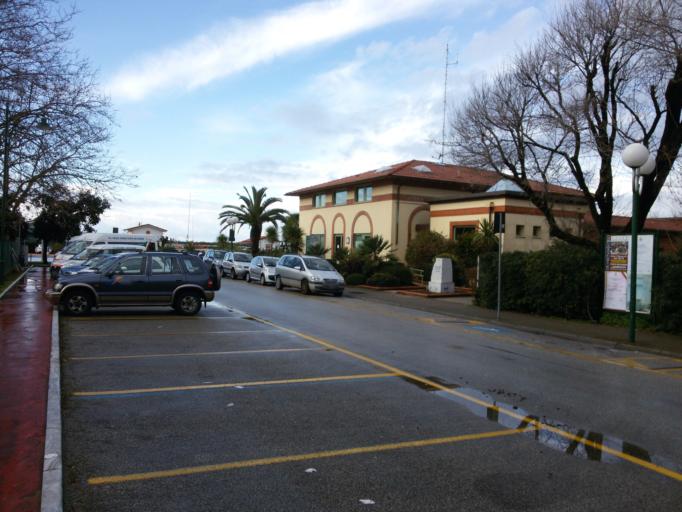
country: IT
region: Tuscany
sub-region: Provincia di Lucca
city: Forte dei Marmi
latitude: 43.9595
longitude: 10.1668
